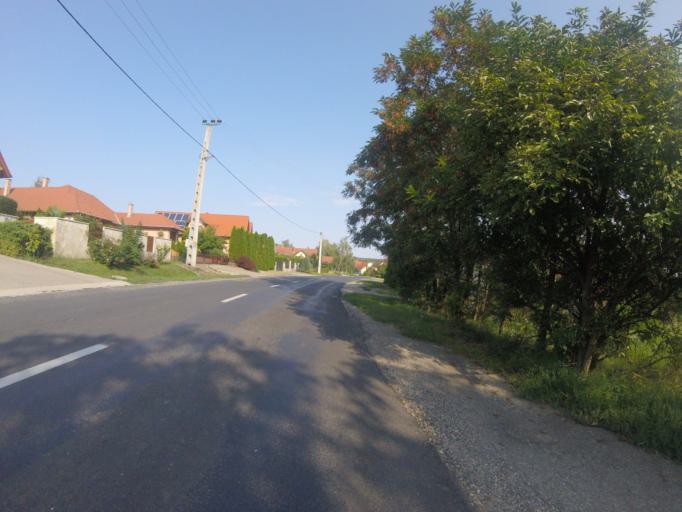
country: HU
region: Gyor-Moson-Sopron
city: Nagycenk
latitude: 47.6437
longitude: 16.6708
